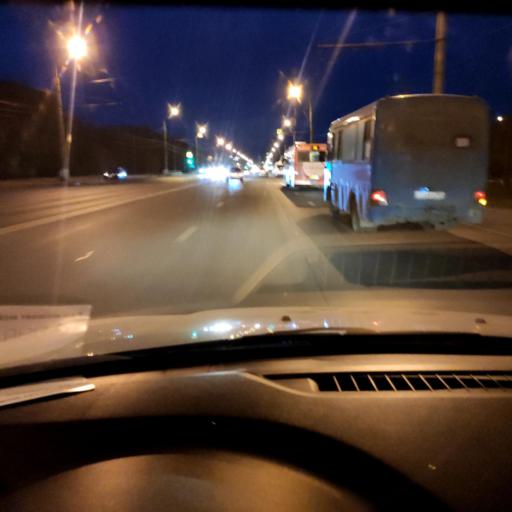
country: RU
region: Samara
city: Tol'yatti
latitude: 53.5522
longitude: 49.3015
